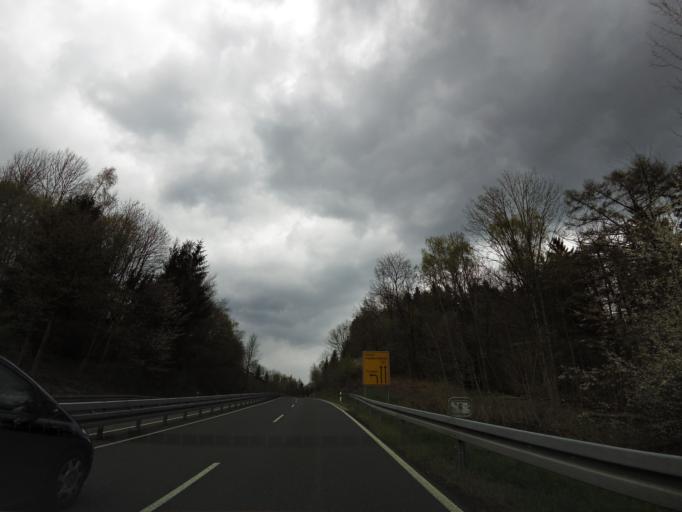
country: DE
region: Lower Saxony
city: Osterode am Harz
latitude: 51.7423
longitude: 10.2799
